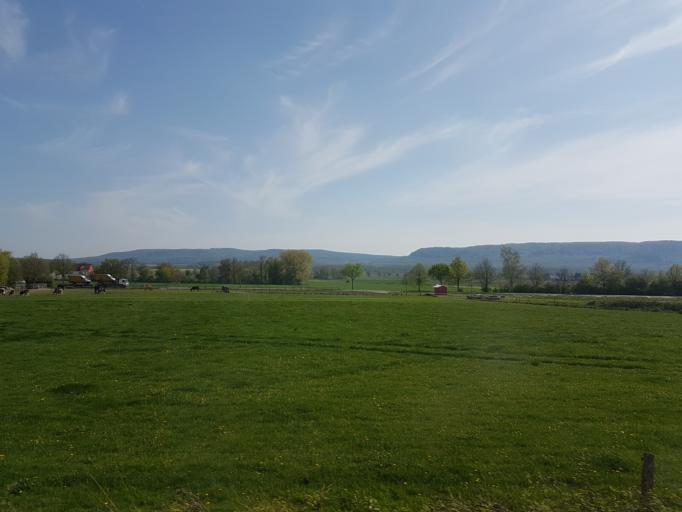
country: DE
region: Lower Saxony
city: Springe
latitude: 52.2123
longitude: 9.6123
